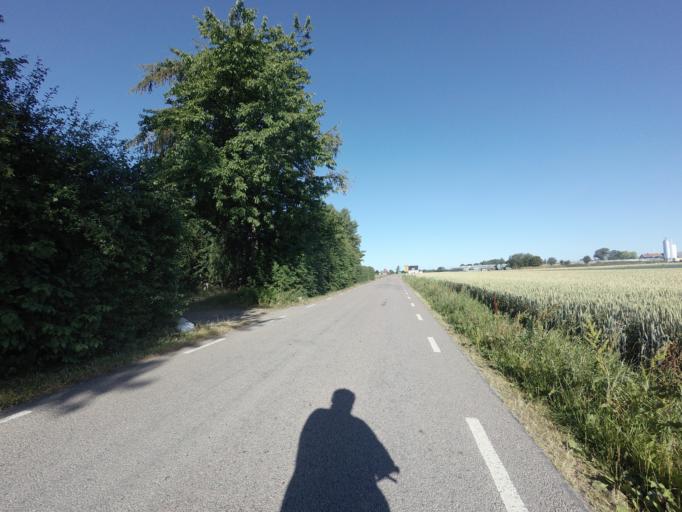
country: SE
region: Skane
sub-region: Hoganas Kommun
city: Hoganas
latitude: 56.1657
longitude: 12.5923
